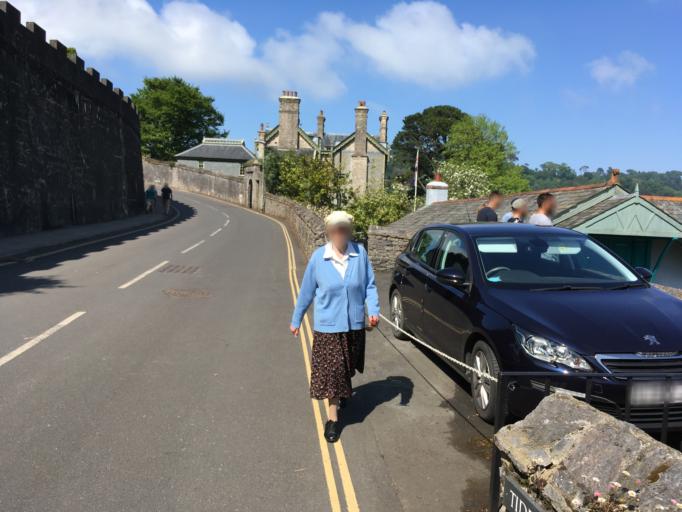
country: GB
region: England
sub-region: Devon
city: Dartmouth
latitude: 50.3431
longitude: -3.5737
